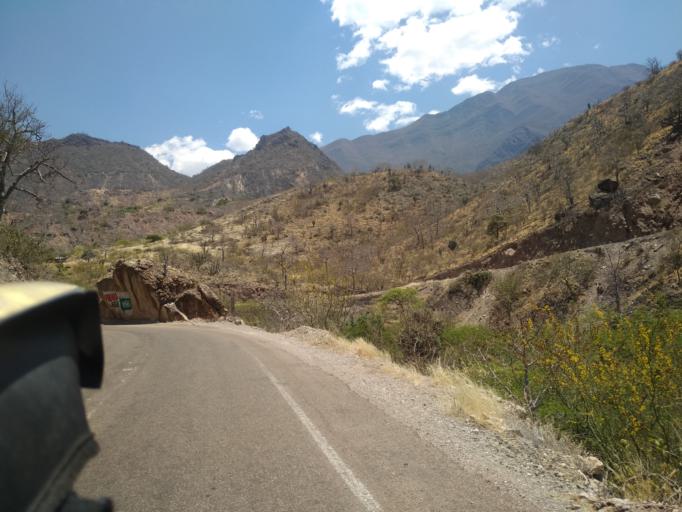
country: PE
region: Amazonas
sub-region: Provincia de Chachapoyas
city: Balsas
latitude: -6.8513
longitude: -78.0398
